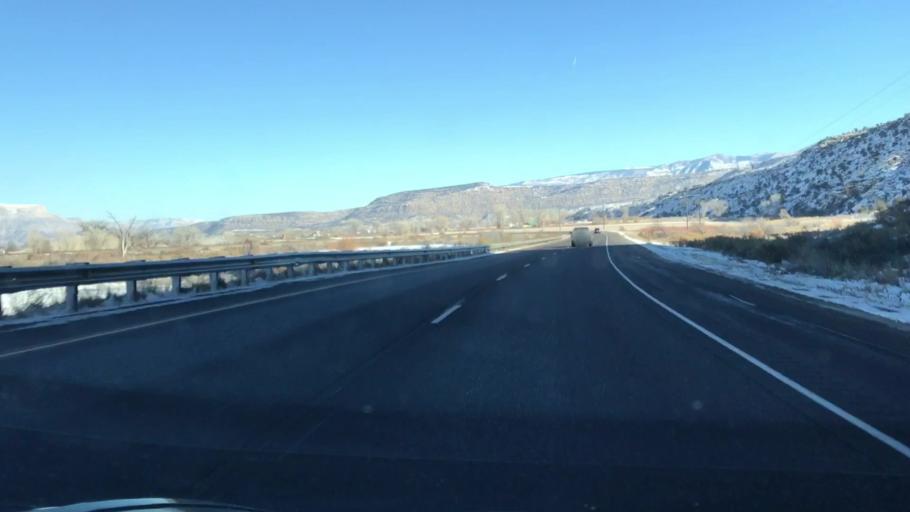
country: US
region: Colorado
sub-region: Mesa County
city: Palisade
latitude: 39.2806
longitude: -108.2363
